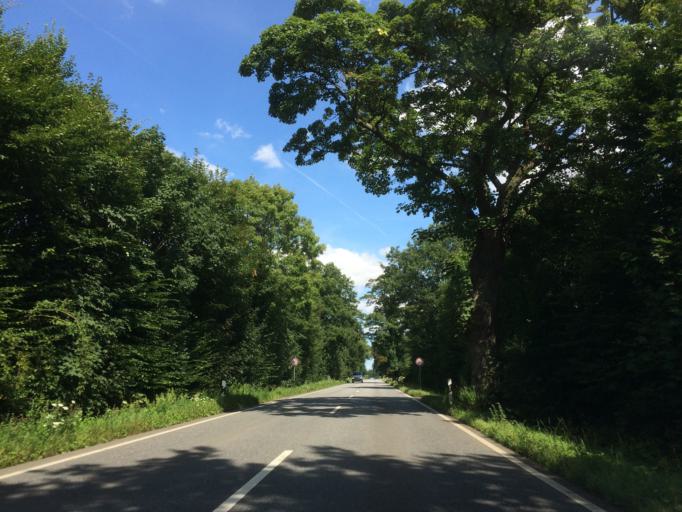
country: DE
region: Schleswig-Holstein
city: Grebin
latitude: 54.1977
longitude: 10.4689
